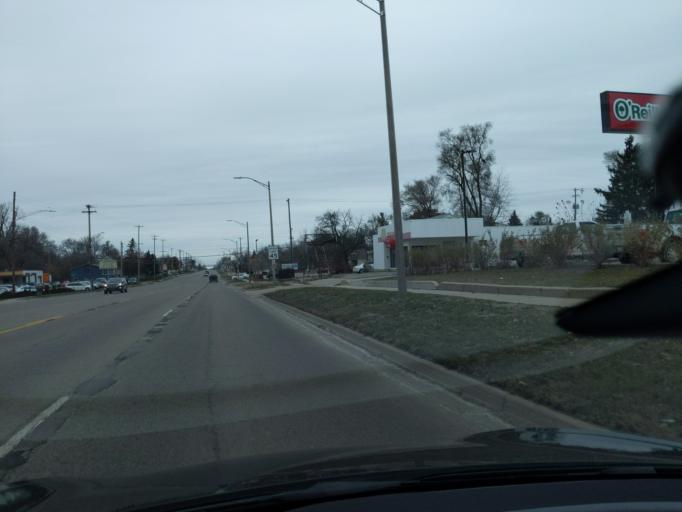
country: US
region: Michigan
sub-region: Ingham County
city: Lansing
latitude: 42.7629
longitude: -84.5427
